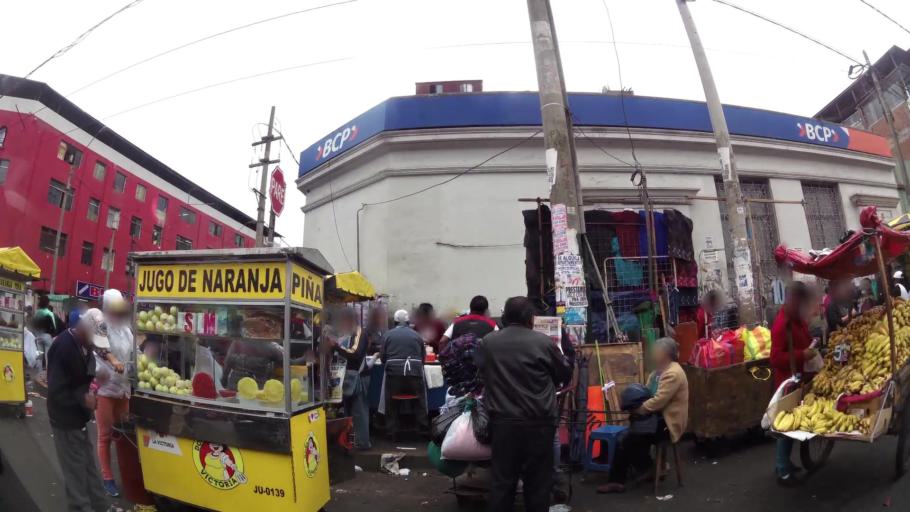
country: PE
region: Lima
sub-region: Lima
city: San Luis
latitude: -12.0636
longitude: -77.0127
